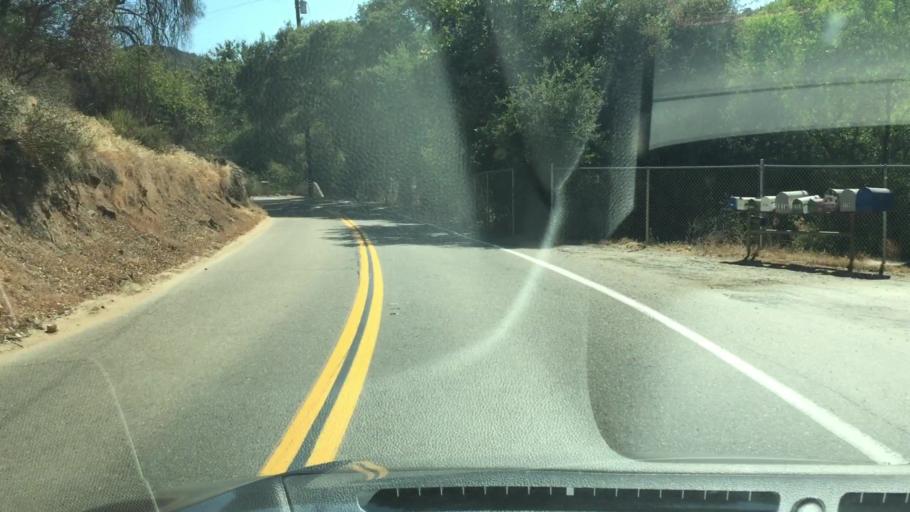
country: US
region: California
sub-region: San Diego County
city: Harbison Canyon
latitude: 32.7539
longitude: -116.7832
